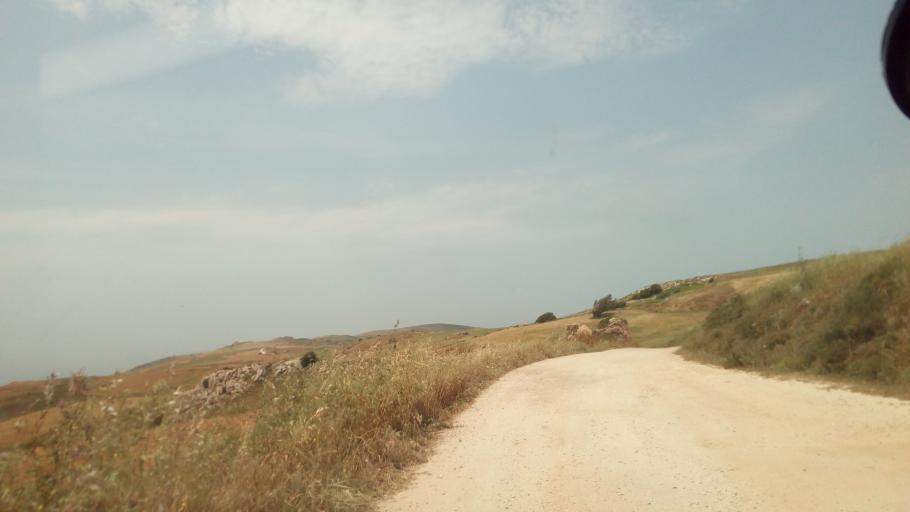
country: CY
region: Pafos
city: Polis
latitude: 34.9729
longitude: 32.3737
